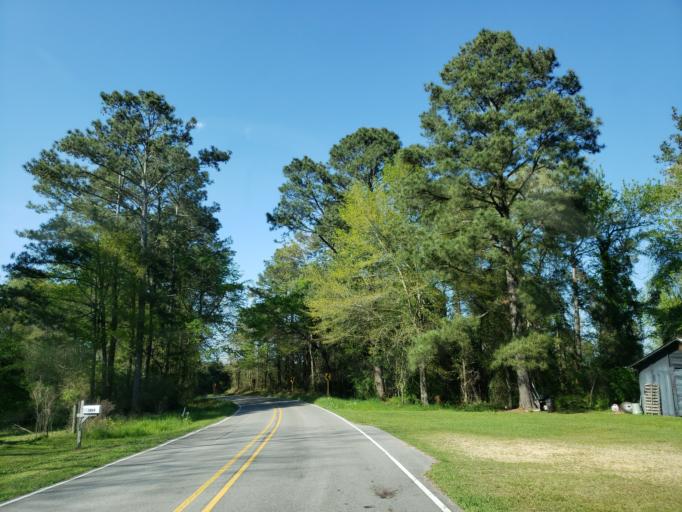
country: US
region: Mississippi
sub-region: Jones County
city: Ellisville
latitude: 31.5968
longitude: -89.3766
